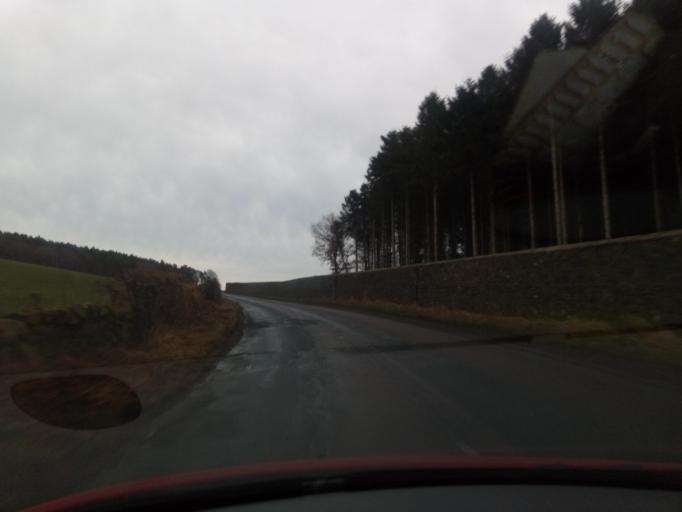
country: GB
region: England
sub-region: Northumberland
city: Alnwick
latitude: 55.4497
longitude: -1.7572
